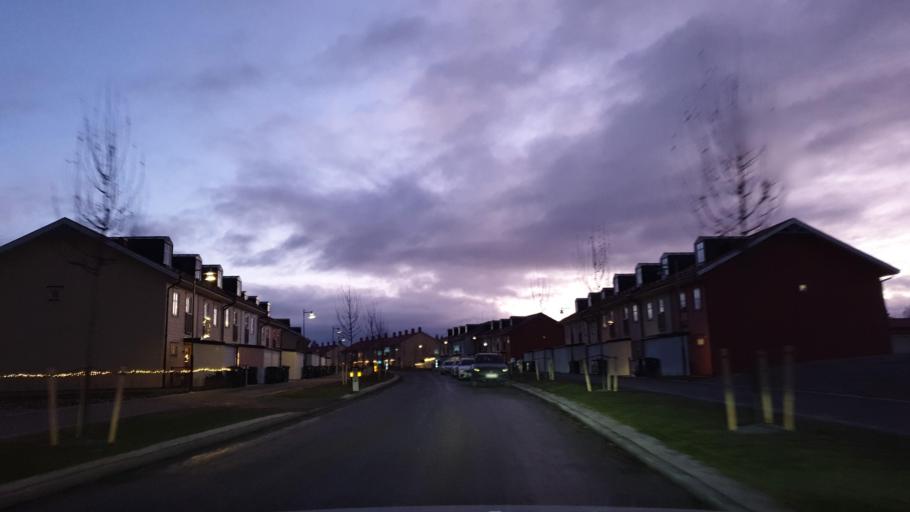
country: SE
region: Stockholm
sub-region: Sigtuna Kommun
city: Marsta
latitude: 59.6117
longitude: 17.7952
